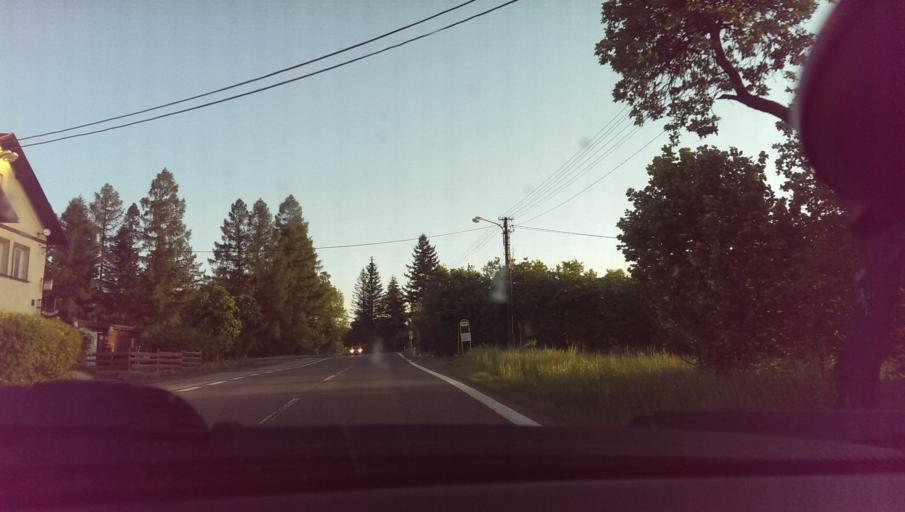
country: CZ
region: Moravskoslezsky
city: Frenstat pod Radhostem
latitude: 49.5338
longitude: 18.2035
